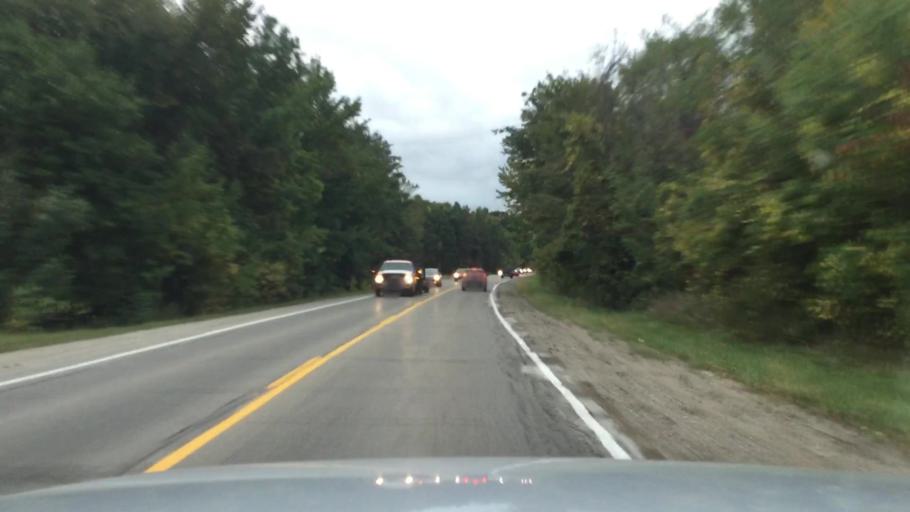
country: US
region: Michigan
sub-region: Livingston County
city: Brighton
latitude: 42.6148
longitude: -83.7485
